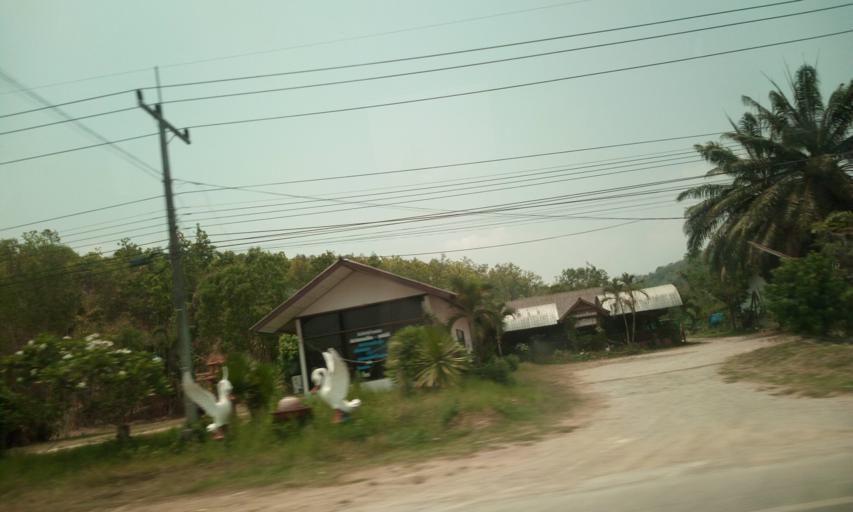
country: TH
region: Chiang Rai
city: Thoeng
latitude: 19.6923
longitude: 100.1693
